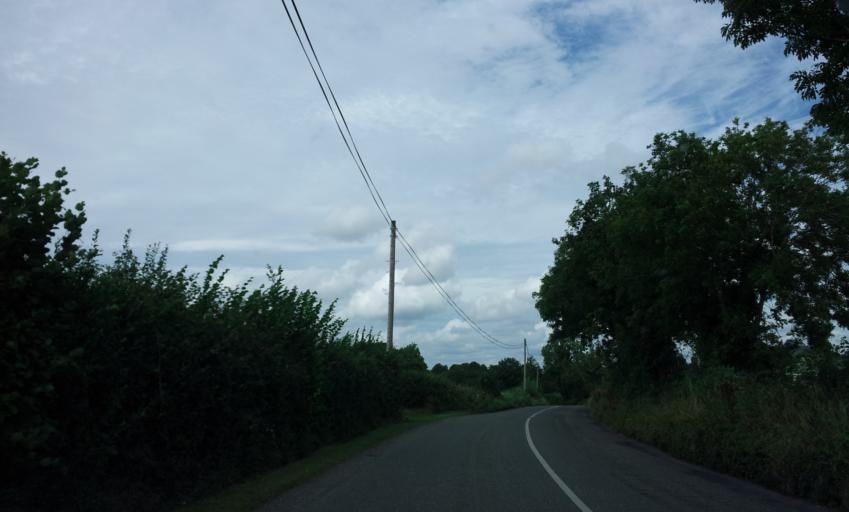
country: IE
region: Leinster
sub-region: Laois
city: Stradbally
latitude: 52.9830
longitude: -7.2168
